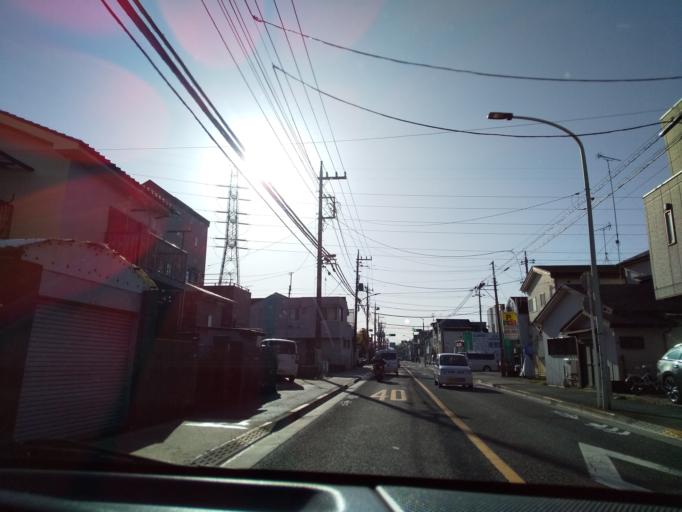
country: JP
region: Tokyo
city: Hino
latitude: 35.7004
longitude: 139.3847
